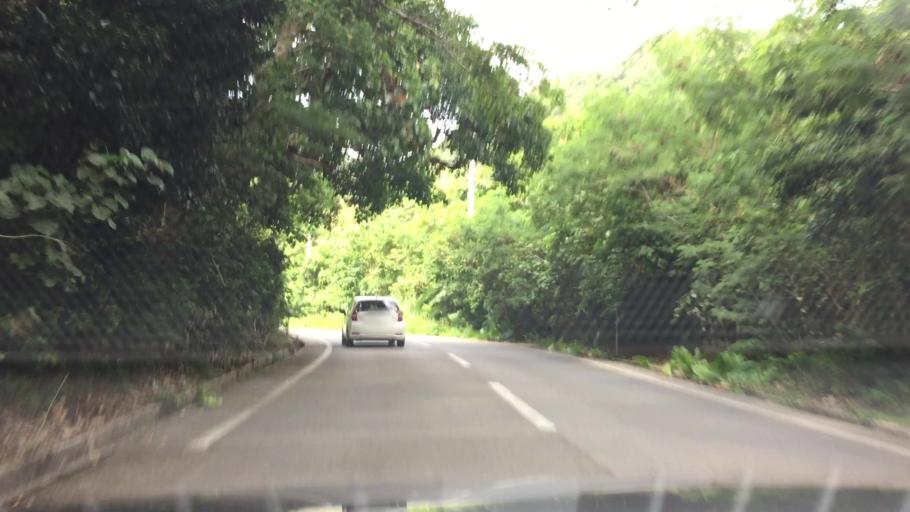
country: JP
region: Okinawa
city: Ishigaki
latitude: 24.4629
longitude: 124.2265
